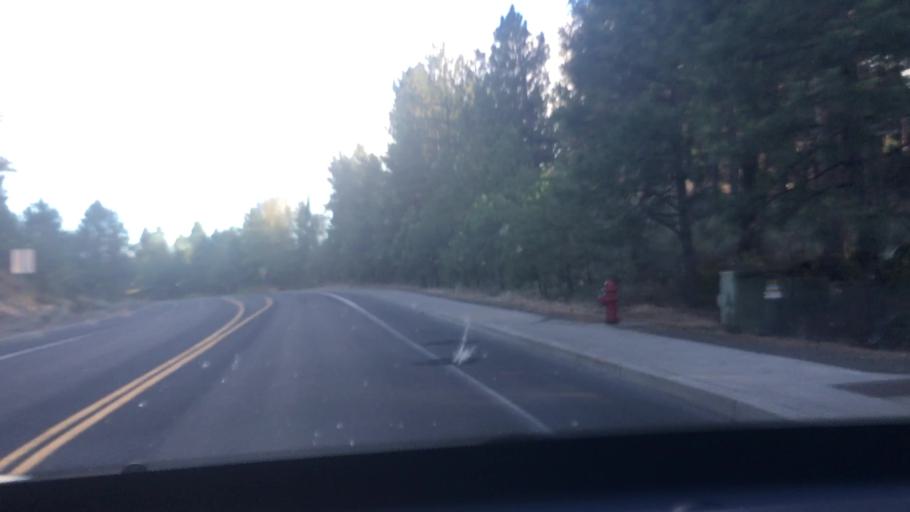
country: US
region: Oregon
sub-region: Deschutes County
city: Bend
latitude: 44.0438
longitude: -121.3442
